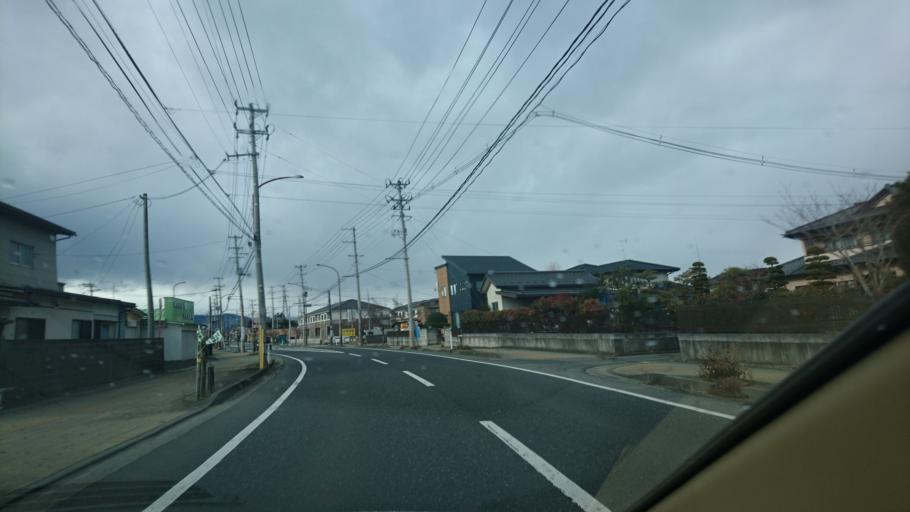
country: JP
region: Miyagi
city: Tomiya
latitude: 38.4422
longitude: 140.9010
